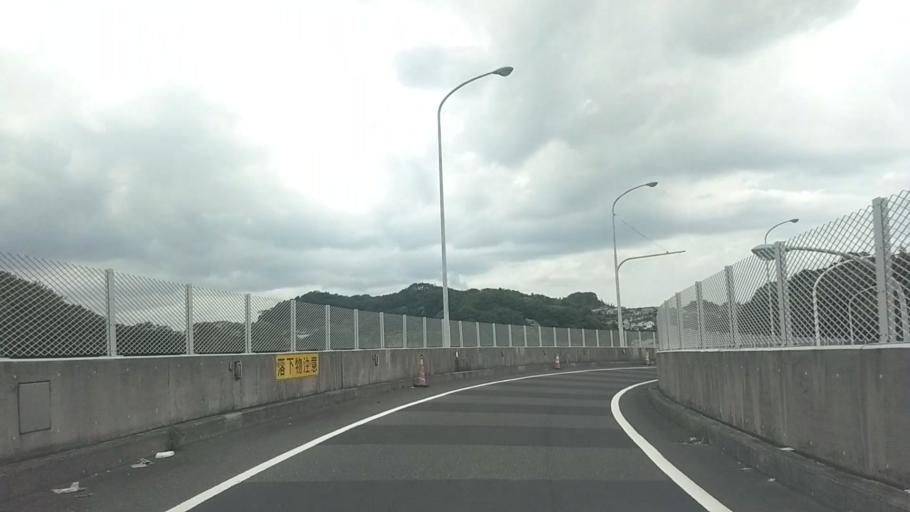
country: JP
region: Kanagawa
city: Fujisawa
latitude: 35.3601
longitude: 139.5093
